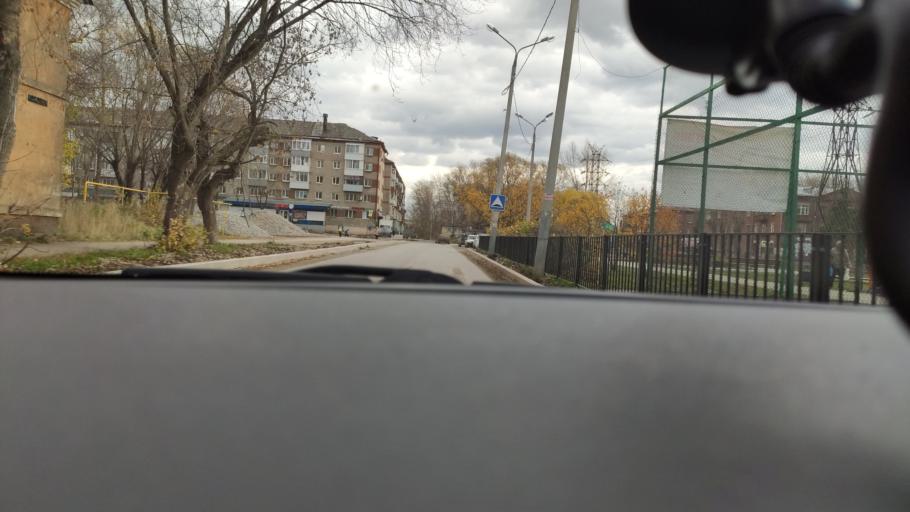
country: RU
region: Perm
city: Perm
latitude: 57.9719
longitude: 56.2733
